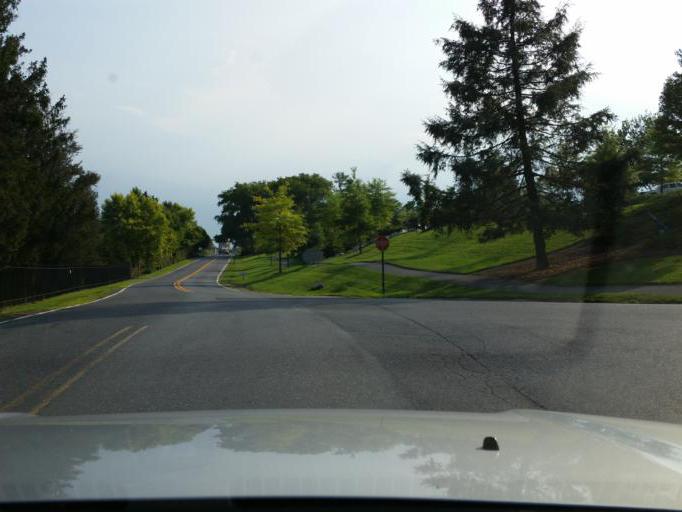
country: US
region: Pennsylvania
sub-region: Dauphin County
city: Hershey
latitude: 40.2994
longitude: -76.6573
